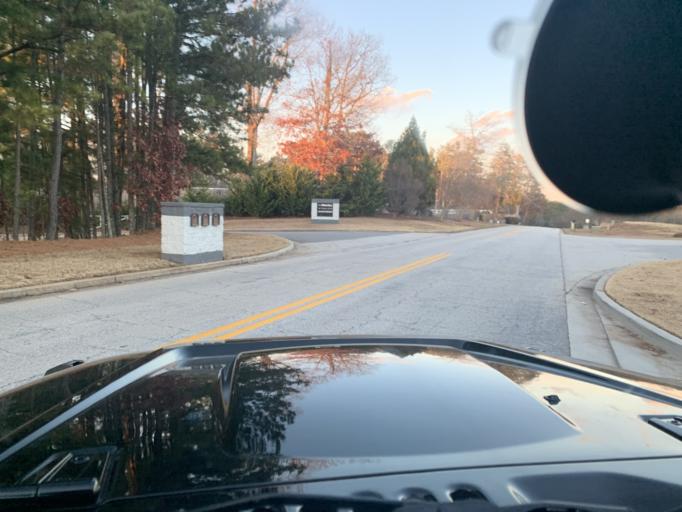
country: US
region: Georgia
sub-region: Fulton County
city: Milton
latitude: 34.1449
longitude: -84.2440
